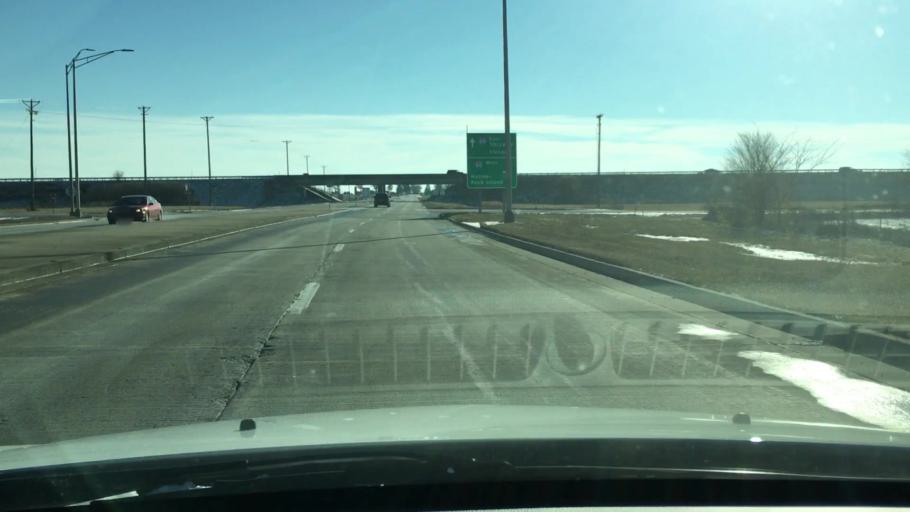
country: US
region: Illinois
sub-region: Ogle County
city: Rochelle
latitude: 41.9028
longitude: -89.0684
